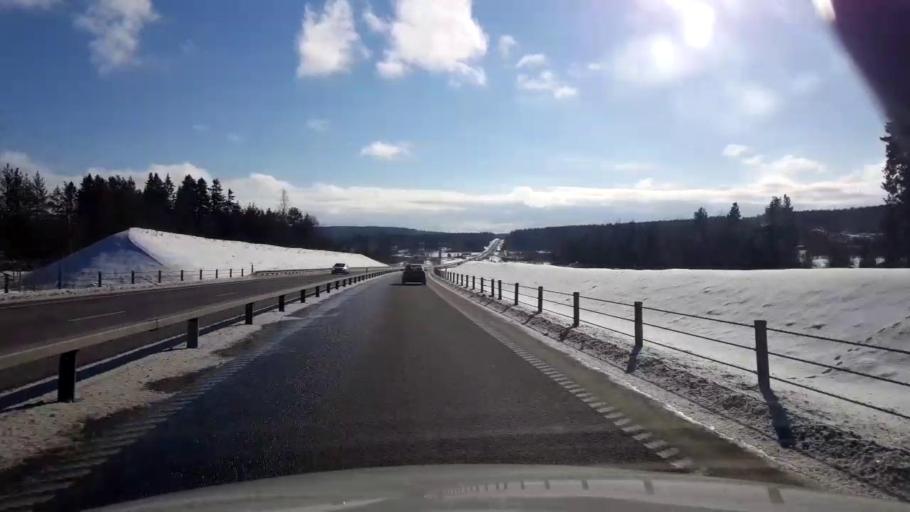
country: SE
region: Vaesternorrland
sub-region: Sundsvalls Kommun
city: Njurundabommen
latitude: 62.2548
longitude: 17.3700
